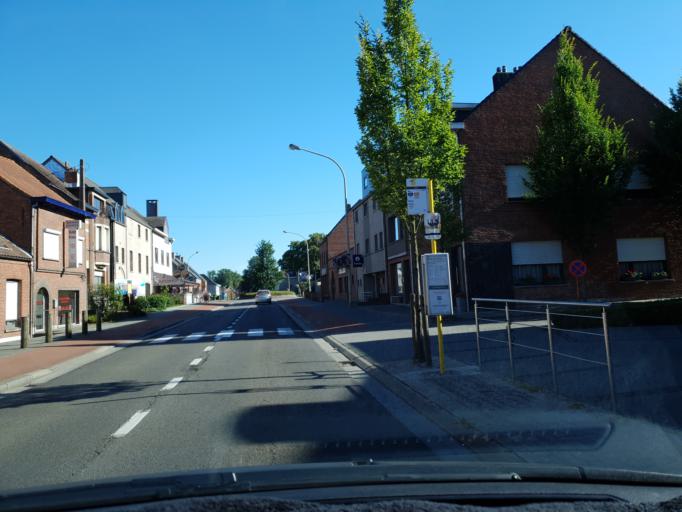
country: BE
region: Flanders
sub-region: Provincie Antwerpen
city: Grobbendonk
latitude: 51.1902
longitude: 4.7386
